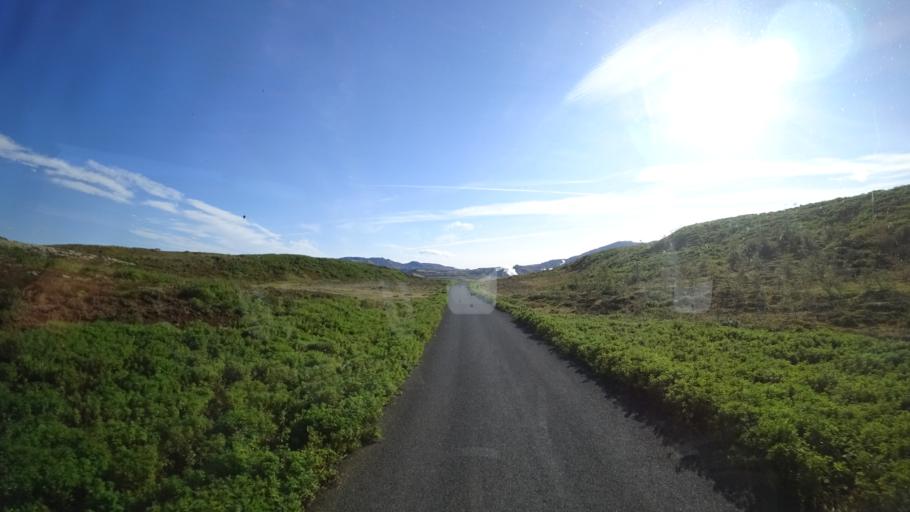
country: IS
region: South
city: Hveragerdi
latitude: 64.1345
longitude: -21.2506
